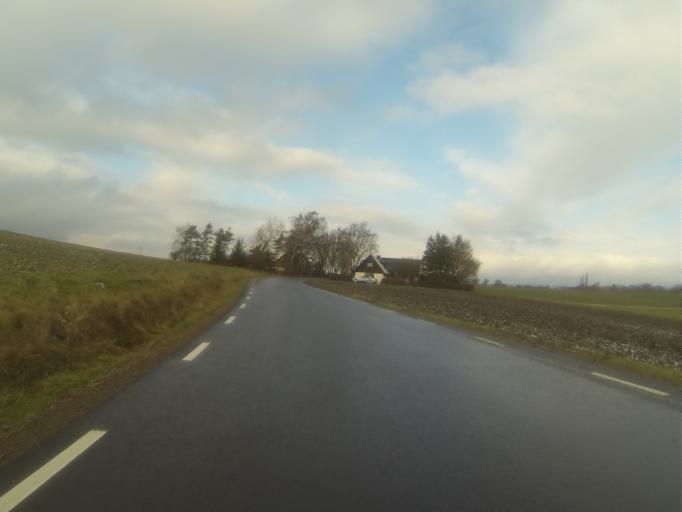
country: SE
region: Skane
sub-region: Svedala Kommun
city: Klagerup
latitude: 55.6188
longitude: 13.3093
